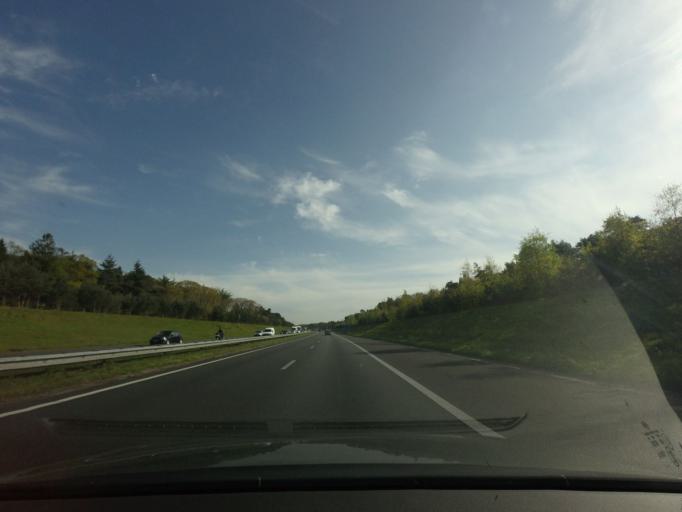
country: NL
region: North Brabant
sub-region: Gemeente Son en Breugel
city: Son
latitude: 51.5205
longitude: 5.4681
